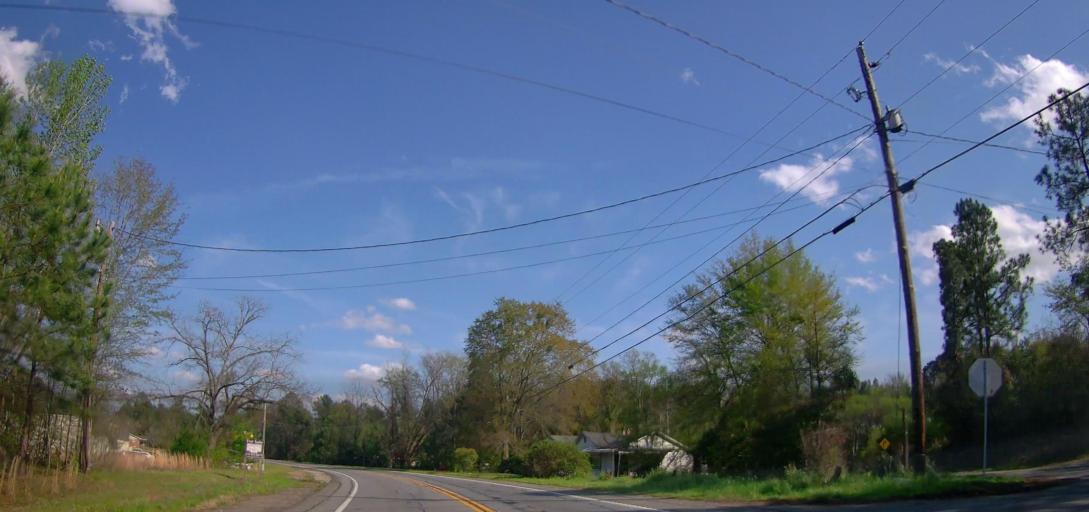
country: US
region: Georgia
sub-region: Baldwin County
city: Hardwick
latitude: 33.0811
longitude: -83.1674
